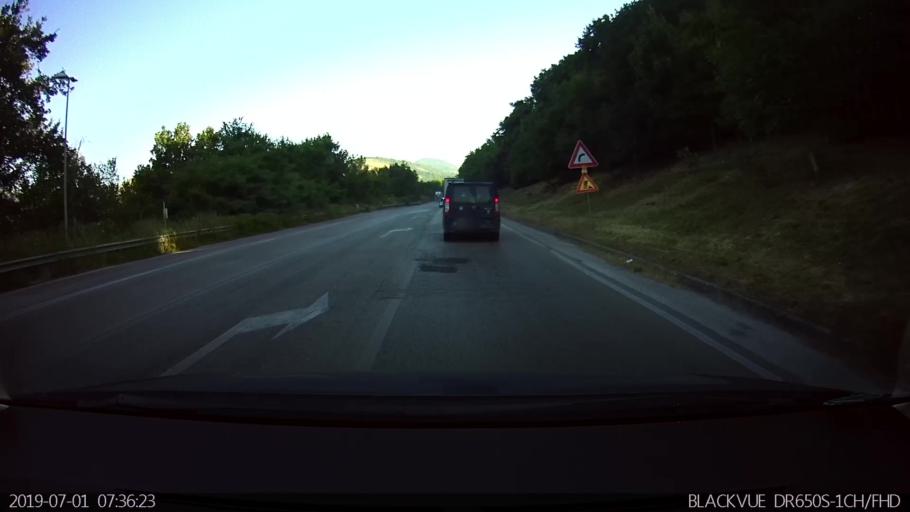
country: IT
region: Latium
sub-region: Provincia di Frosinone
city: Giuliano di Roma
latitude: 41.5312
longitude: 13.2672
